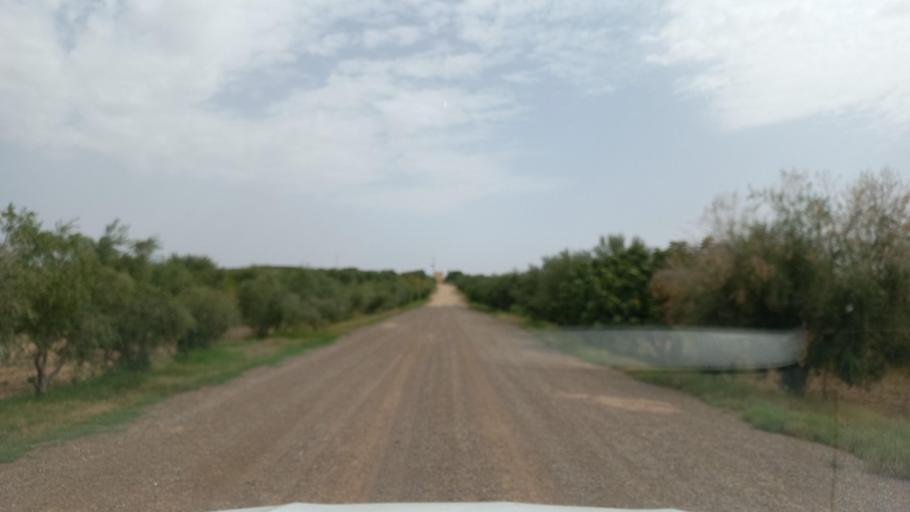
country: TN
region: Al Qasrayn
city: Kasserine
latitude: 35.2710
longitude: 9.0084
